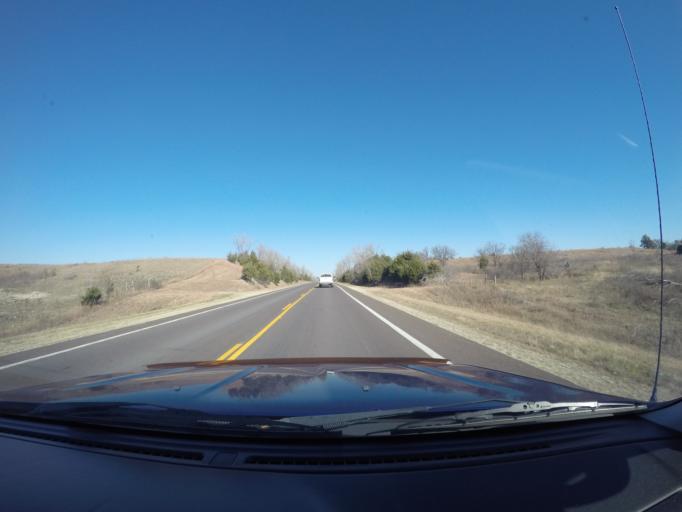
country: US
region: Kansas
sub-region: Marshall County
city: Blue Rapids
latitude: 39.4798
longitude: -96.7546
